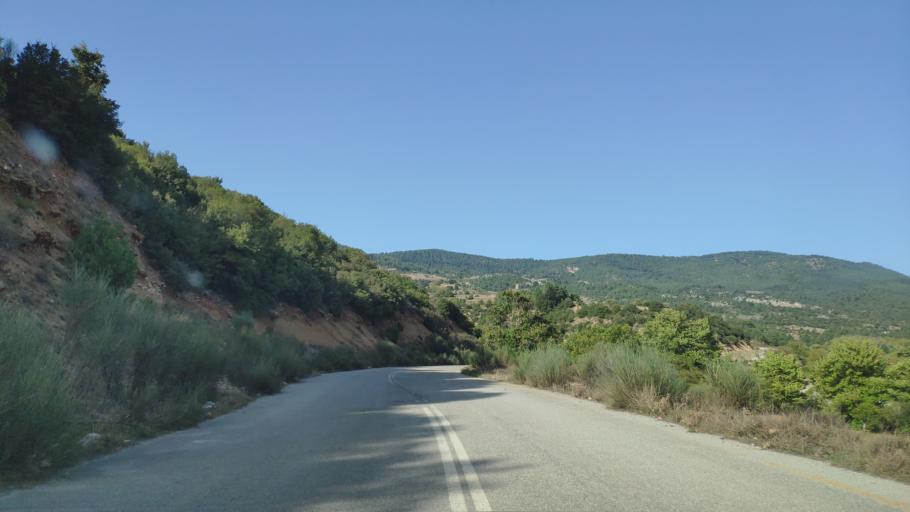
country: GR
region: West Greece
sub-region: Nomos Achaias
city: Aiyira
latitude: 37.9864
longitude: 22.3599
